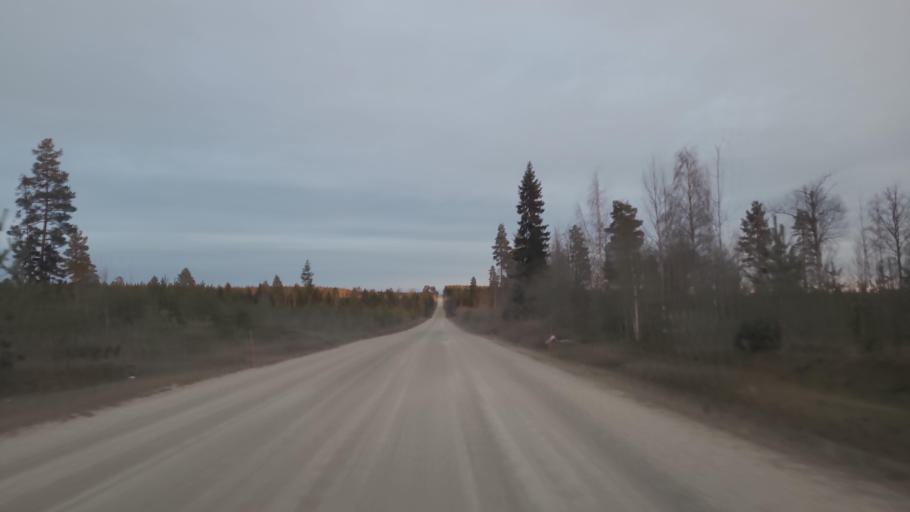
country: FI
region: Lapland
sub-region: Kemi-Tornio
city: Tervola
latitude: 66.0648
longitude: 24.9132
